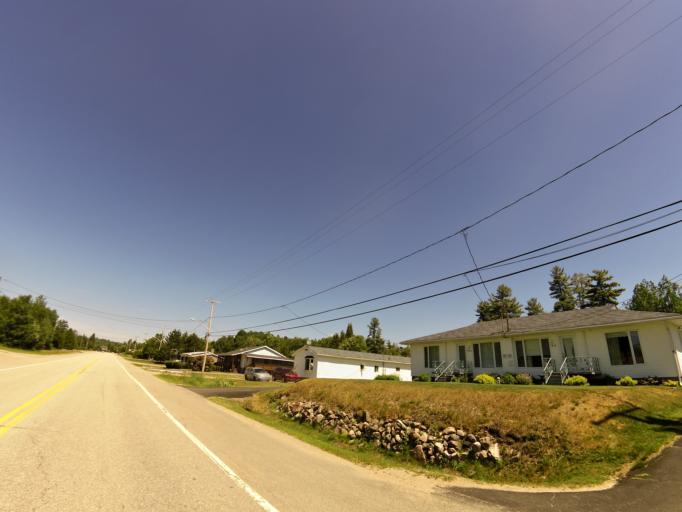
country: CA
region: Quebec
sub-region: Abitibi-Temiscamingue
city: Temiscaming
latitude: 46.7423
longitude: -79.0689
